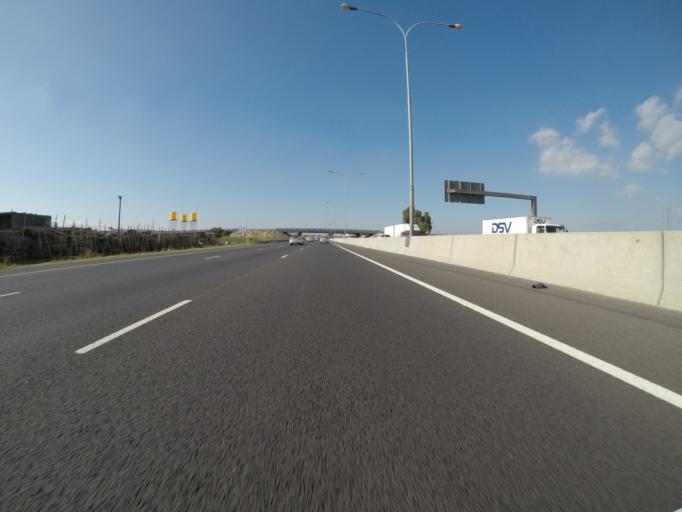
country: ZA
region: Western Cape
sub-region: City of Cape Town
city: Kraaifontein
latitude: -33.9093
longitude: 18.6714
